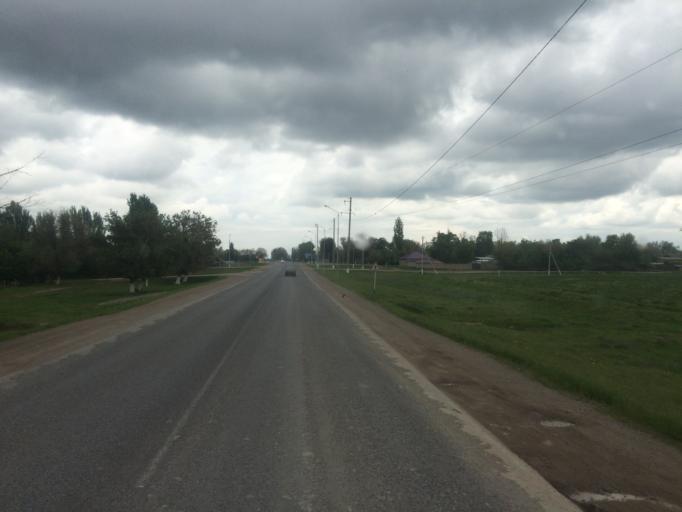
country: KZ
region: Zhambyl
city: Georgiyevka
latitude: 43.1445
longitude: 74.6143
